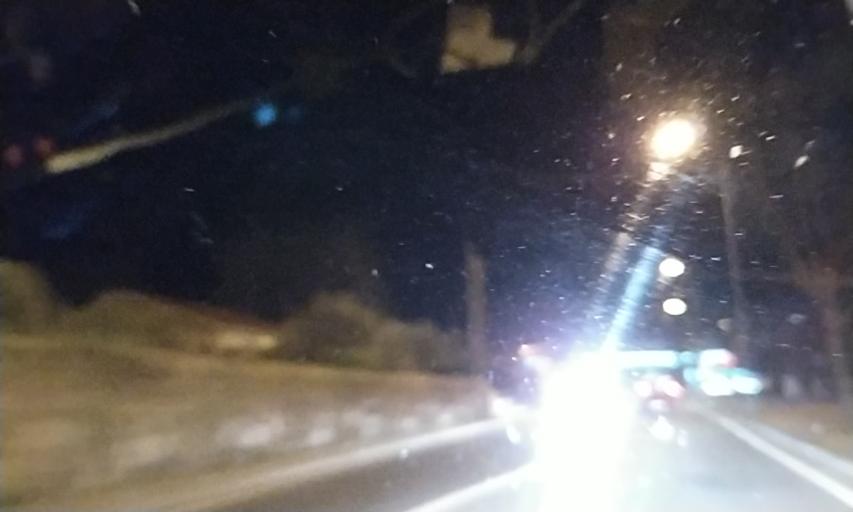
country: PT
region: Castelo Branco
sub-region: Concelho do Fundao
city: Fundao
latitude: 40.1583
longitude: -7.4974
